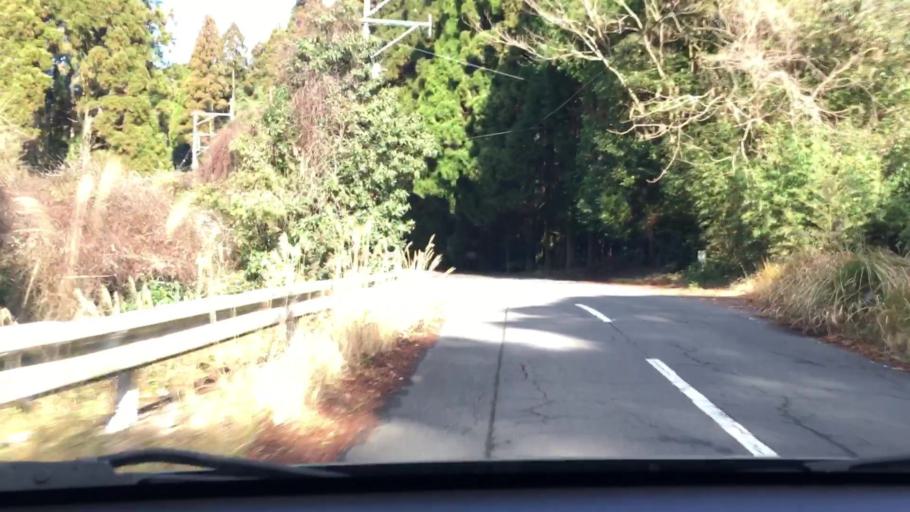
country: JP
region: Kagoshima
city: Ijuin
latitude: 31.7292
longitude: 130.4192
